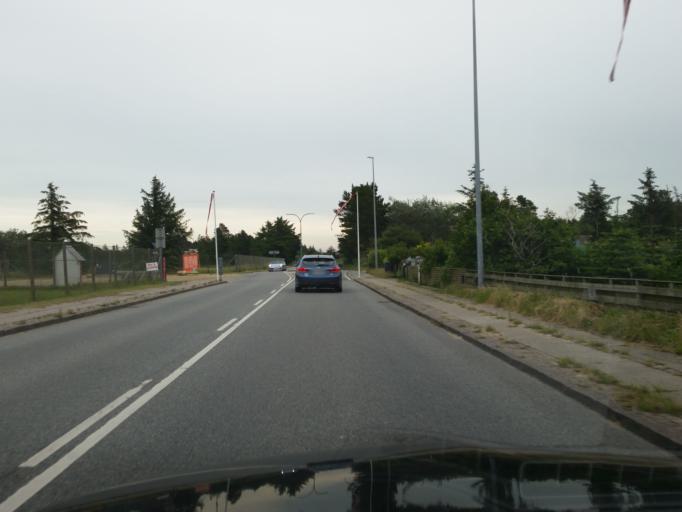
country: DK
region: Central Jutland
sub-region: Ringkobing-Skjern Kommune
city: Hvide Sande
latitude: 55.8163
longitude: 8.2020
